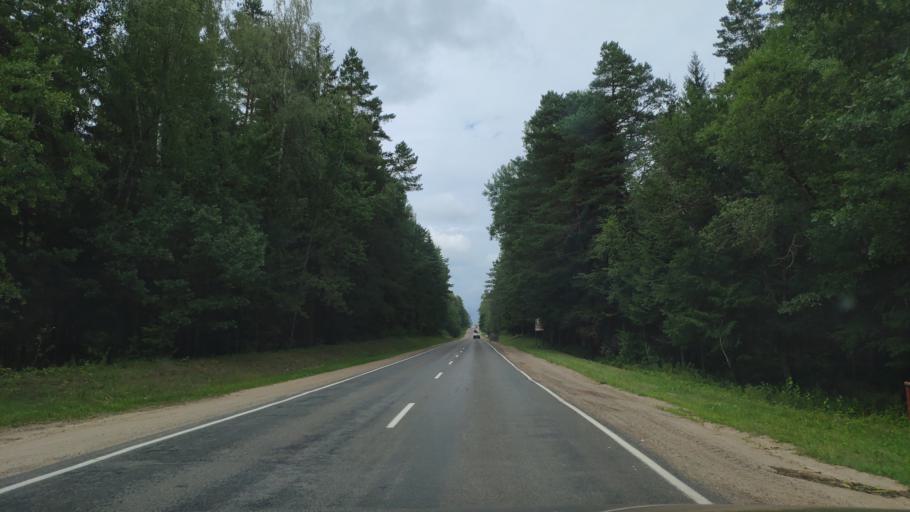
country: BY
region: Minsk
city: Novosel'ye
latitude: 53.9365
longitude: 27.2440
